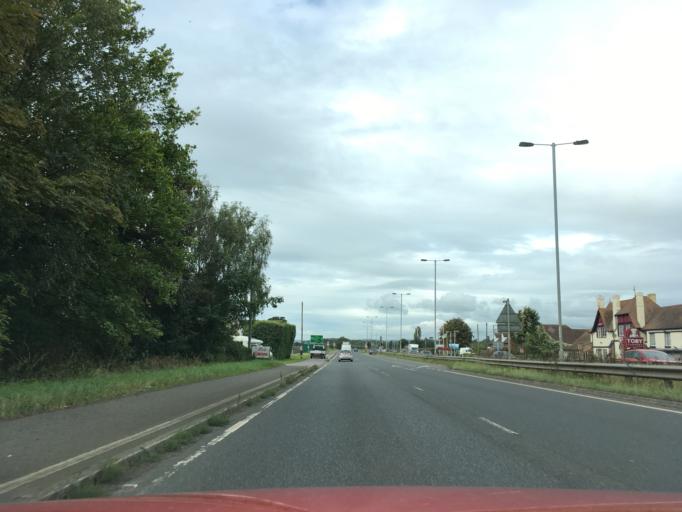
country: GB
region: England
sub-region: Gloucestershire
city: Gloucester
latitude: 51.8742
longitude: -2.2722
